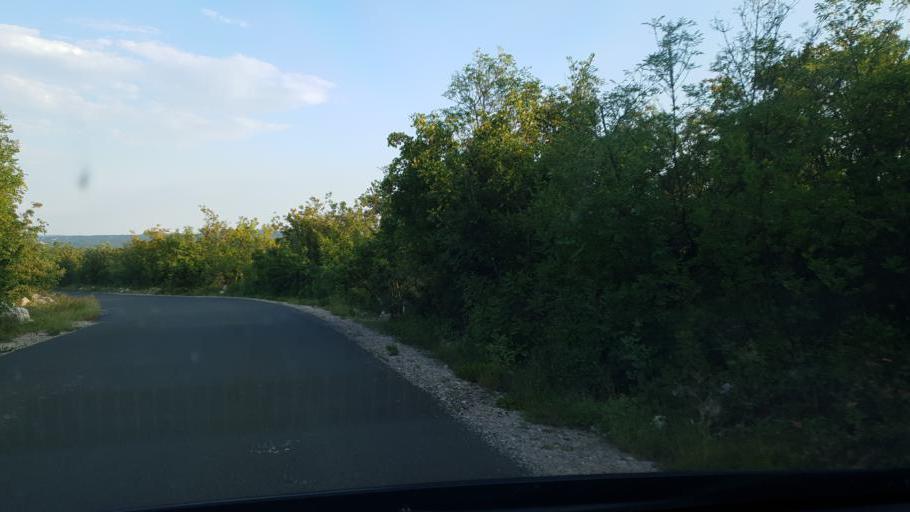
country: HR
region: Primorsko-Goranska
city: Omisalj
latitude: 45.1909
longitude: 14.5845
